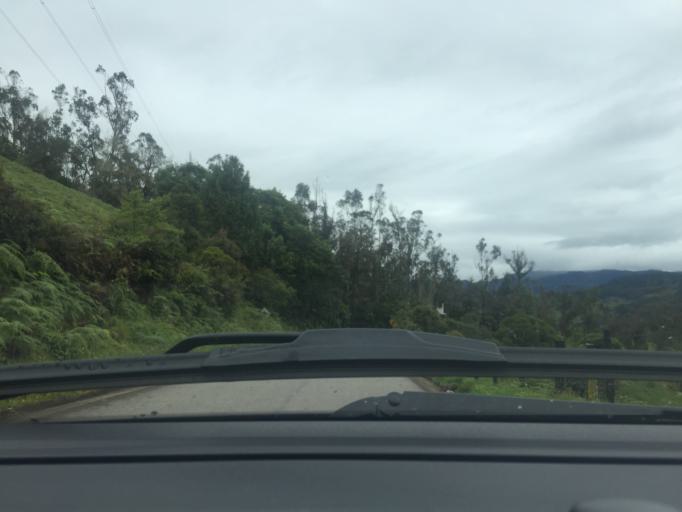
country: CO
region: Cundinamarca
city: Junin
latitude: 4.8202
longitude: -73.7496
